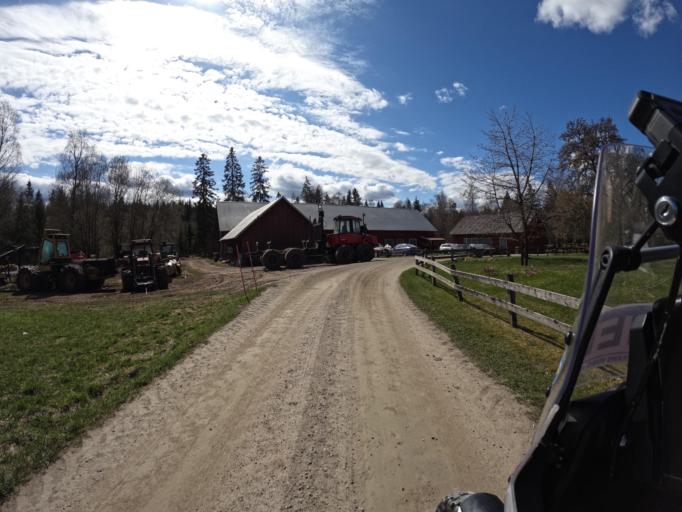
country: SE
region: Vaestra Goetaland
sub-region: Ulricehamns Kommun
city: Ulricehamn
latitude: 57.9069
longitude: 13.4166
